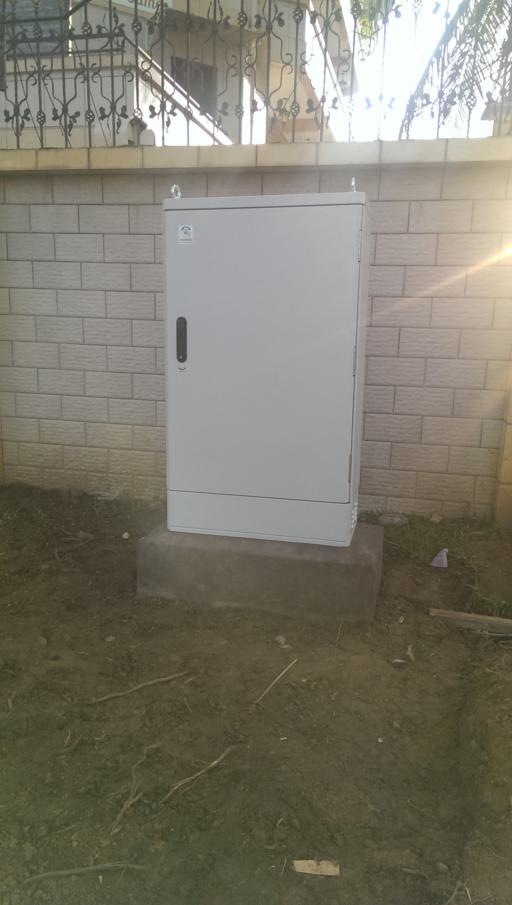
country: CM
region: Littoral
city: Douala
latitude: 4.0901
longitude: 9.7377
